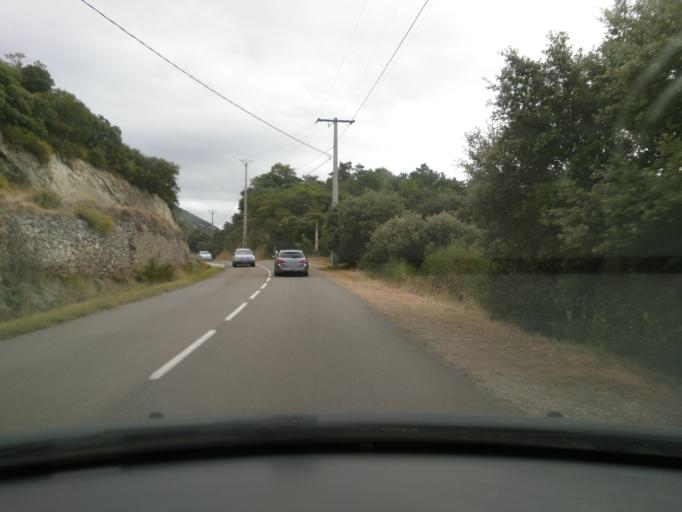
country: FR
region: Provence-Alpes-Cote d'Azur
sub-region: Departement du Vaucluse
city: Valreas
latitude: 44.4166
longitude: 5.0668
